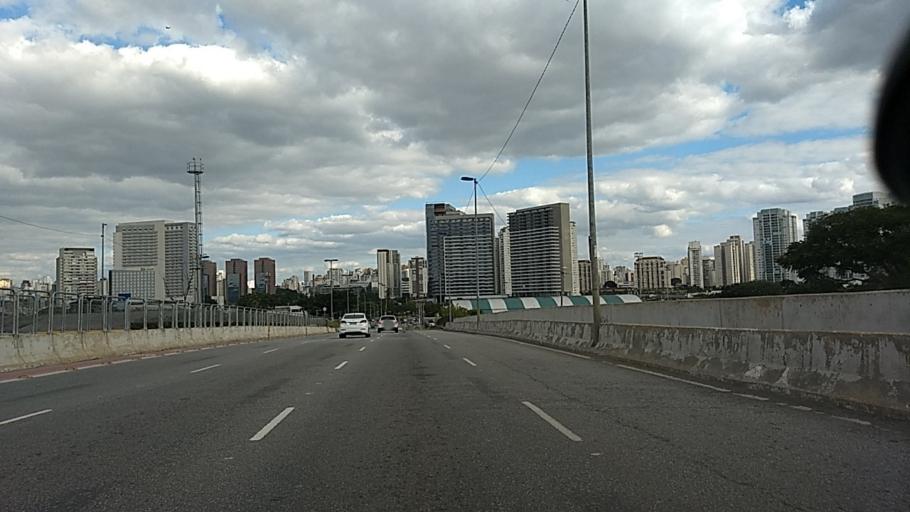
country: BR
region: Sao Paulo
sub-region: Sao Paulo
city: Sao Paulo
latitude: -23.5136
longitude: -46.6791
